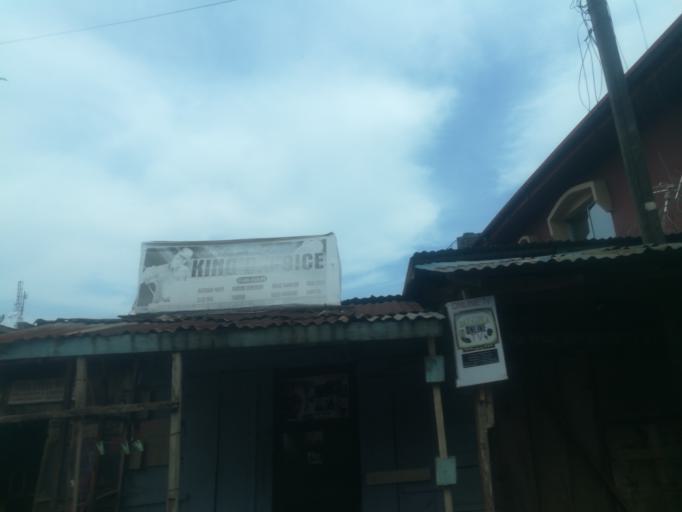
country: NG
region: Oyo
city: Ibadan
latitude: 7.4140
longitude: 3.8963
